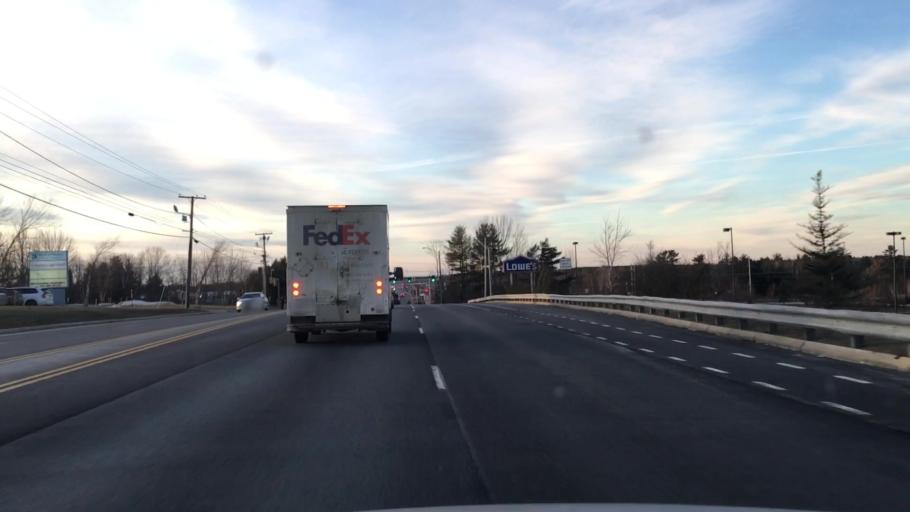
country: US
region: Maine
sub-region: Penobscot County
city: Brewer
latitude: 44.7732
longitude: -68.7259
